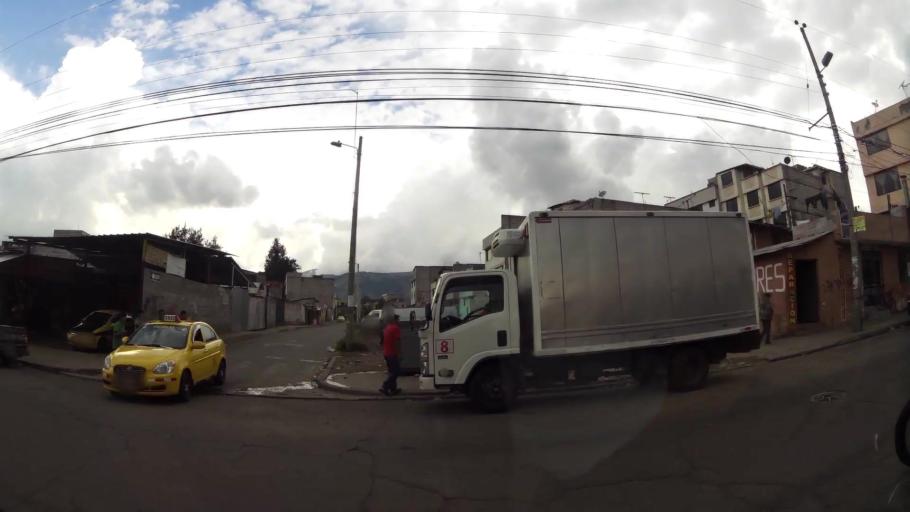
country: EC
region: Pichincha
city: Quito
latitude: -0.2745
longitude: -78.5368
